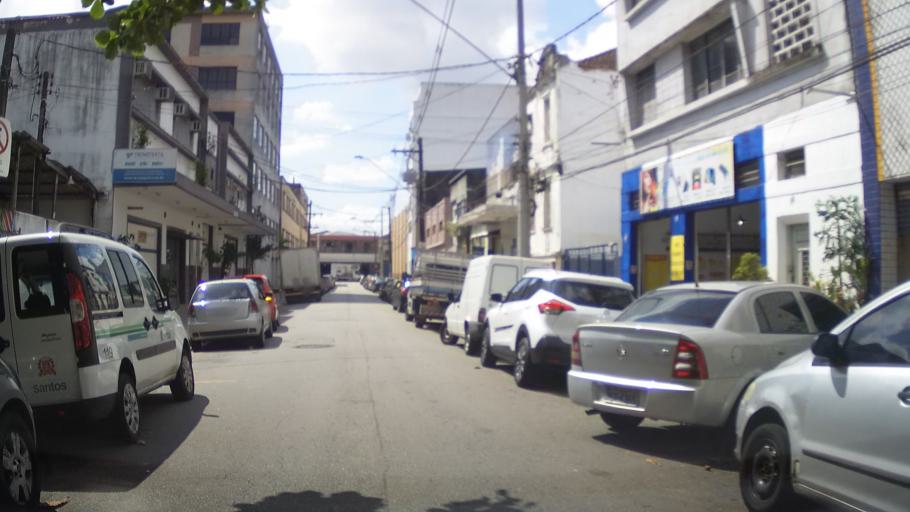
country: BR
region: Sao Paulo
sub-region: Santos
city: Santos
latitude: -23.9431
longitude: -46.3247
